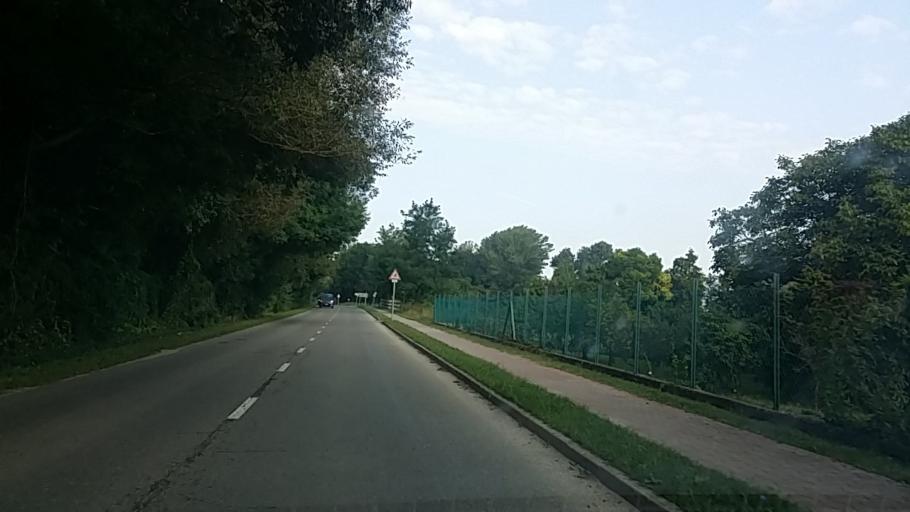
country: HU
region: Gyor-Moson-Sopron
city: Nagycenk
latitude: 47.6274
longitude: 16.7401
